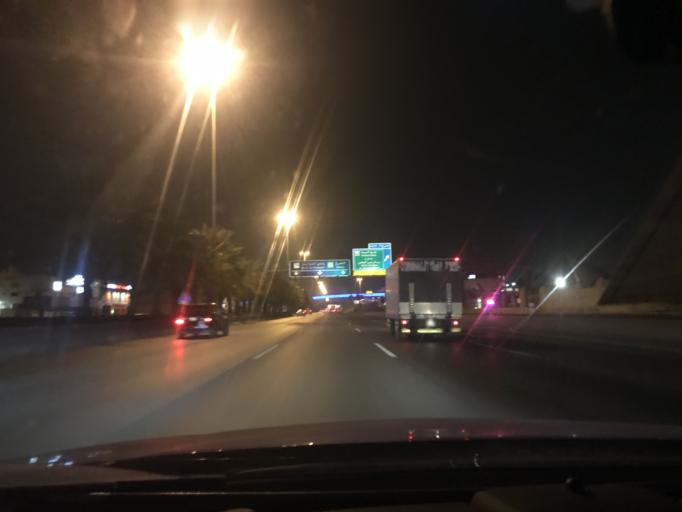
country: SA
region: Ar Riyad
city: Riyadh
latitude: 24.7425
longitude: 46.7460
